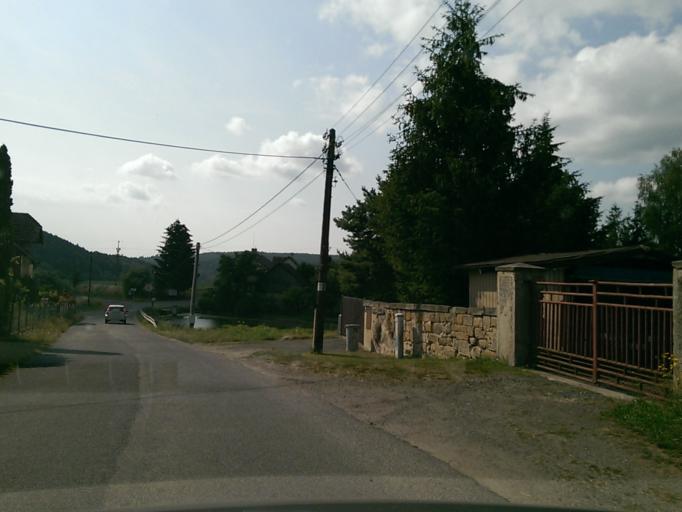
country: CZ
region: Central Bohemia
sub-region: Okres Mlada Boleslav
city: Zd'ar
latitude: 50.5433
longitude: 15.1216
